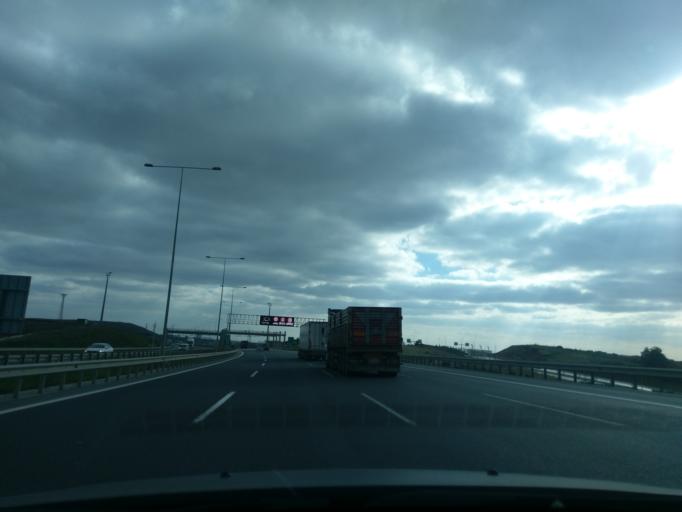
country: TR
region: Istanbul
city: Basaksehir
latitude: 41.1294
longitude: 28.8060
